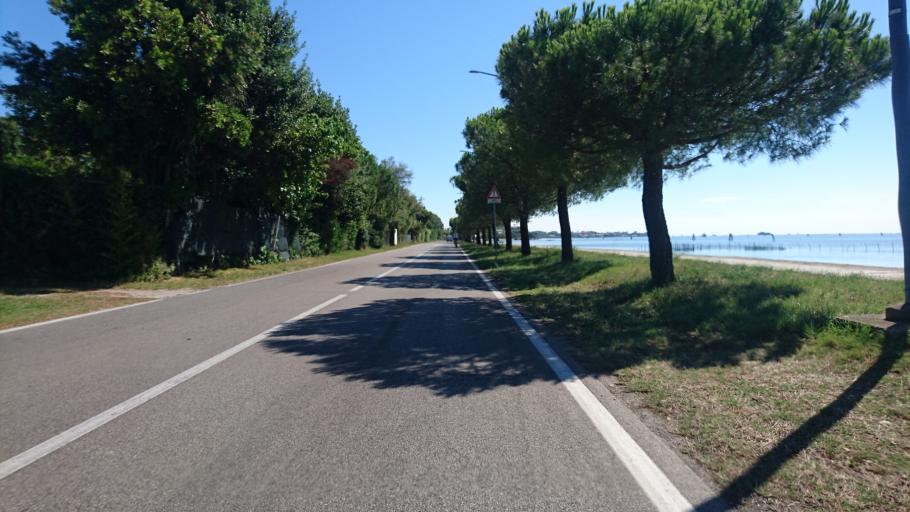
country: IT
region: Veneto
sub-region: Provincia di Venezia
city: San Pietro in Volta
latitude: 45.3638
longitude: 12.3337
